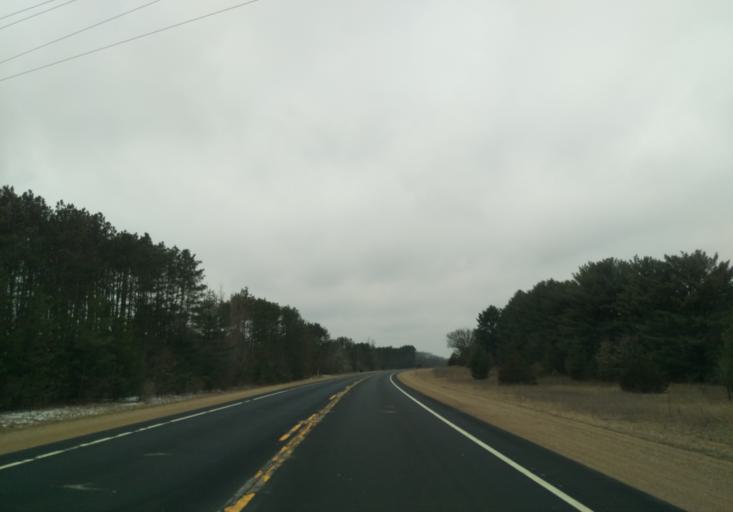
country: US
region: Wisconsin
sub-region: Sauk County
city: Spring Green
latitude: 43.1917
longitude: -90.2196
